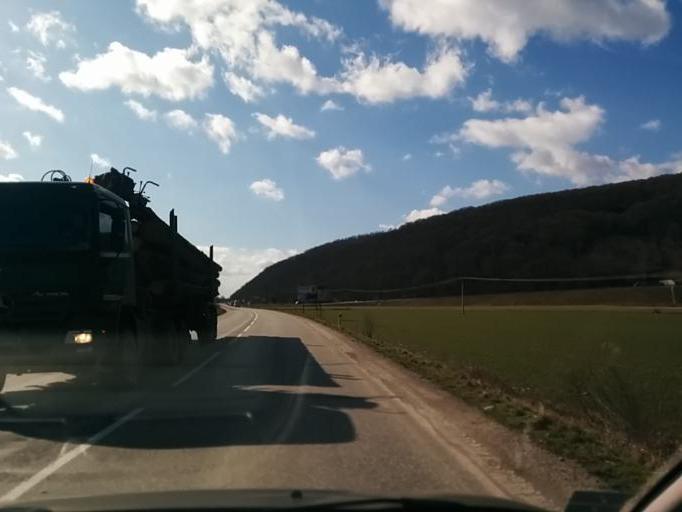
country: SK
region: Trenciansky
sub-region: Okres Nove Mesto nad Vahom
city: Nove Mesto nad Vahom
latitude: 48.7954
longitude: 17.8696
